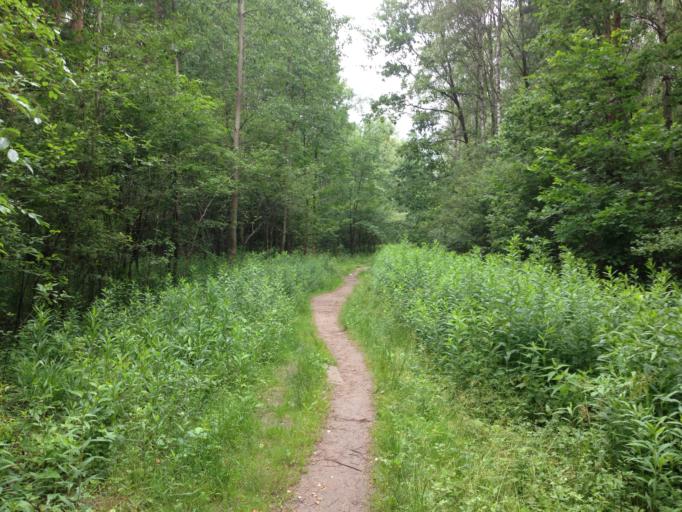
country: PL
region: Masovian Voivodeship
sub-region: Powiat warszawski zachodni
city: Babice
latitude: 52.2637
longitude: 20.8729
